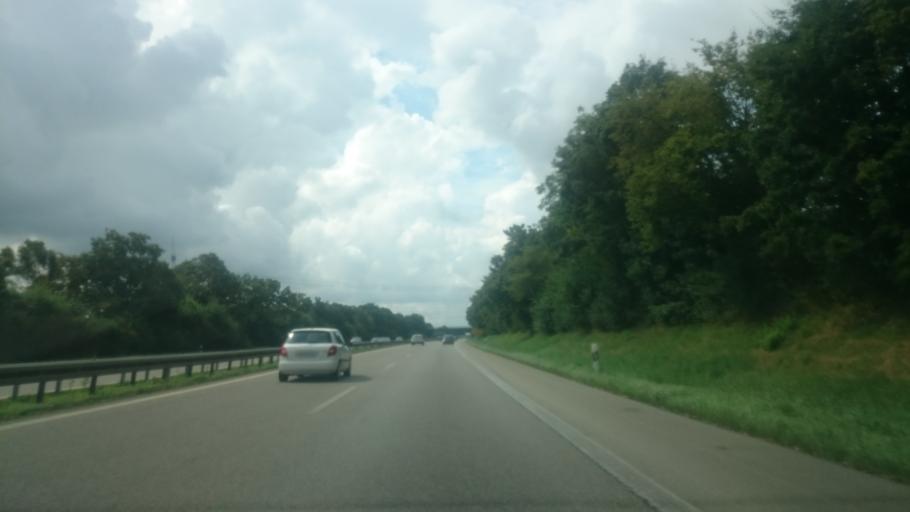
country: DE
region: Bavaria
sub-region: Swabia
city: Oberottmarshausen
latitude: 48.2367
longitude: 10.8689
